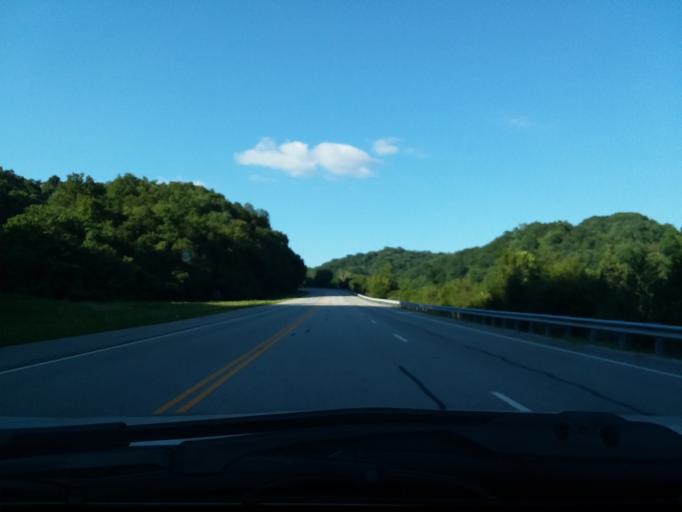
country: US
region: Tennessee
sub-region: Clay County
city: Celina
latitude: 36.5533
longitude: -85.4542
